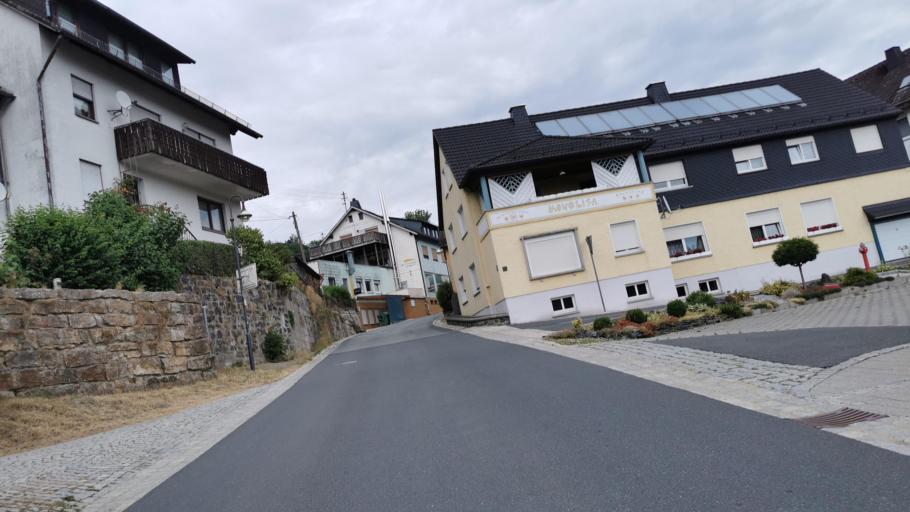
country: DE
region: Bavaria
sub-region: Upper Franconia
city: Steinwiesen
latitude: 50.3235
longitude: 11.4697
